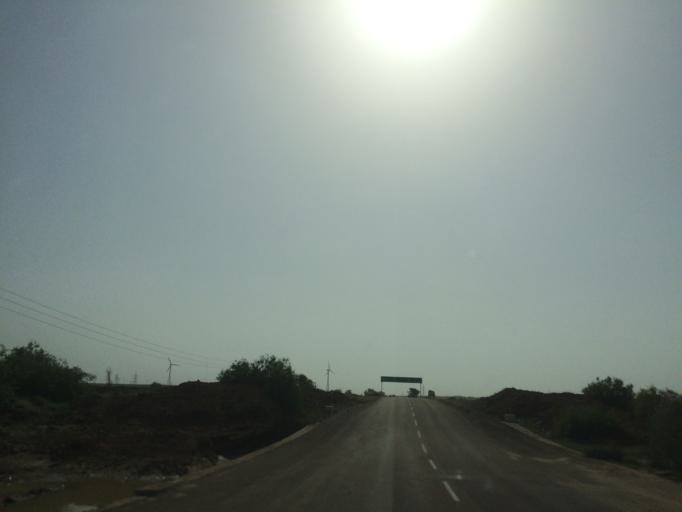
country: IN
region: Rajasthan
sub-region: Jaisalmer
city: Jaisalmer
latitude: 26.9190
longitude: 70.7926
